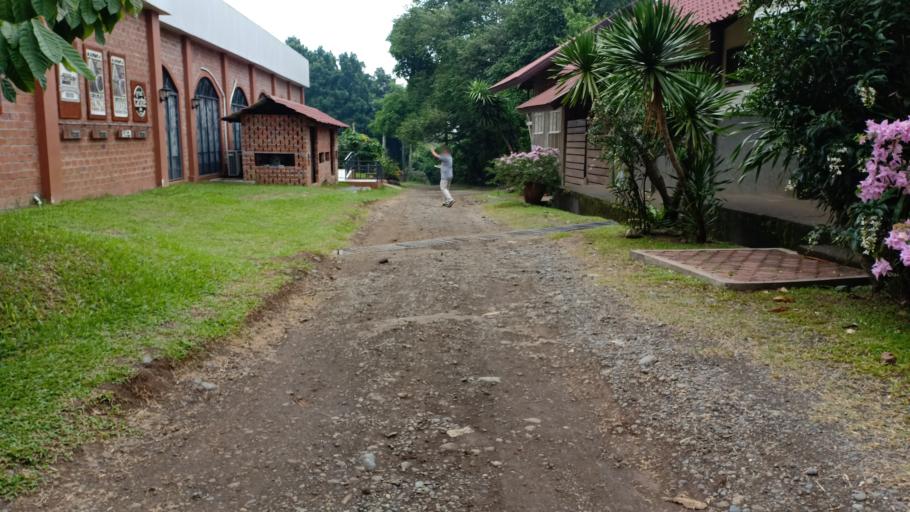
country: PH
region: Davao
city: Malagos
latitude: 7.1915
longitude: 125.4277
